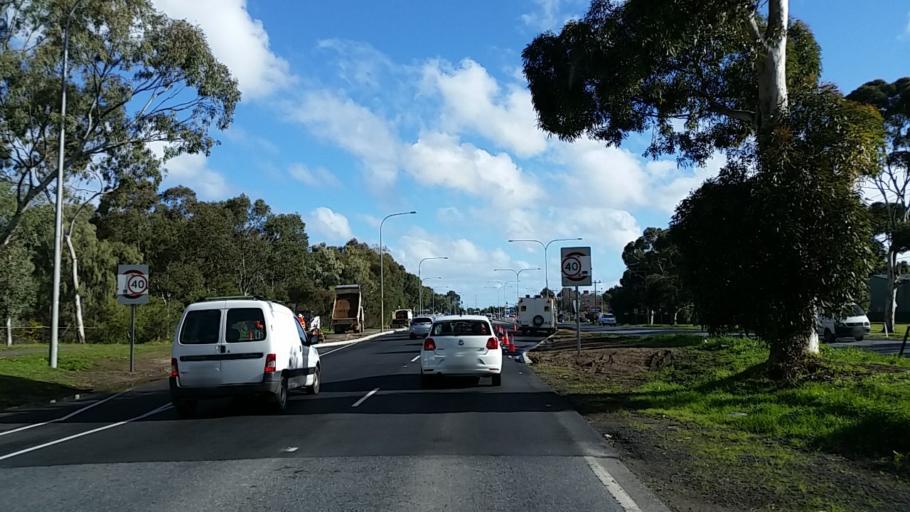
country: AU
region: South Australia
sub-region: Salisbury
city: Ingle Farm
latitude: -34.8222
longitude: 138.6198
